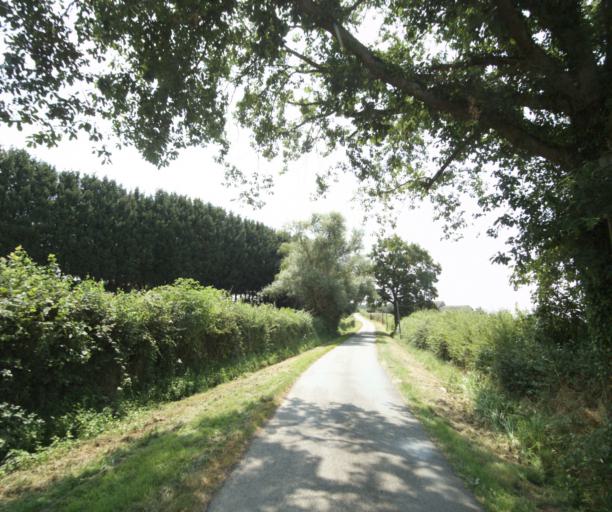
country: FR
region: Bourgogne
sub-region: Departement de Saone-et-Loire
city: Gueugnon
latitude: 46.5672
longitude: 4.0601
